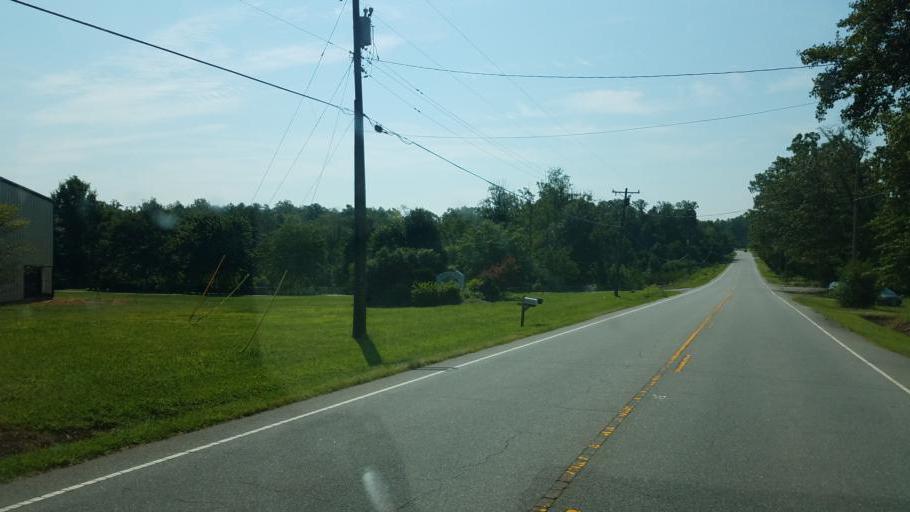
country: US
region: North Carolina
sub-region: Burke County
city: Glen Alpine
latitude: 35.7997
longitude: -81.7719
